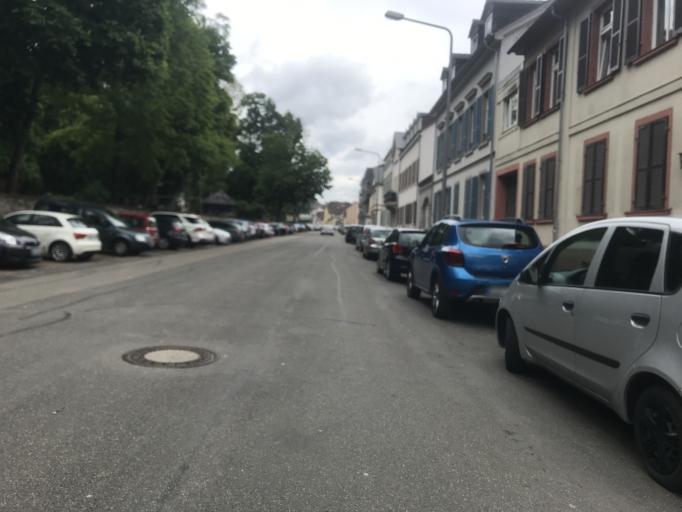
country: DE
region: Hesse
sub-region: Regierungsbezirk Darmstadt
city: Wiesbaden
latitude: 50.0425
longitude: 8.2381
